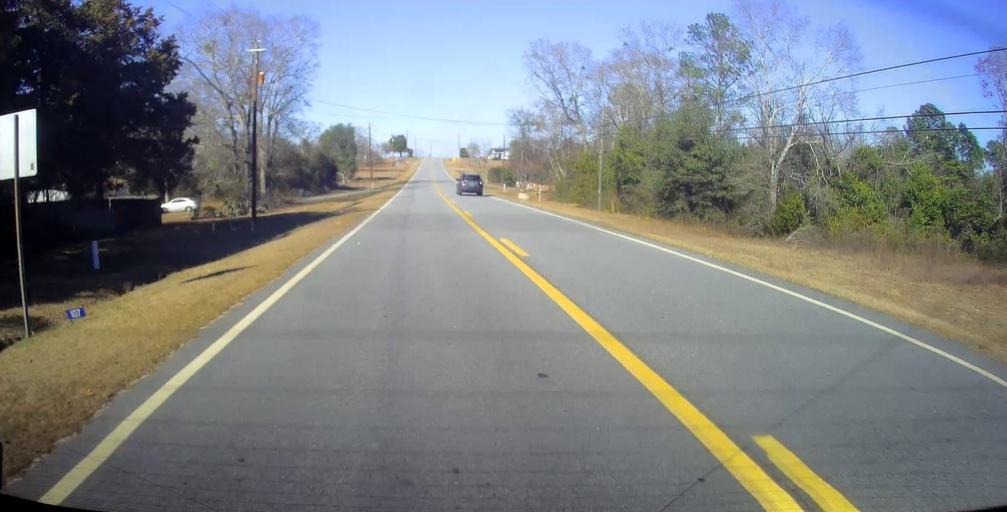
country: US
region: Georgia
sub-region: Taylor County
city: Butler
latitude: 32.5645
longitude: -84.2241
